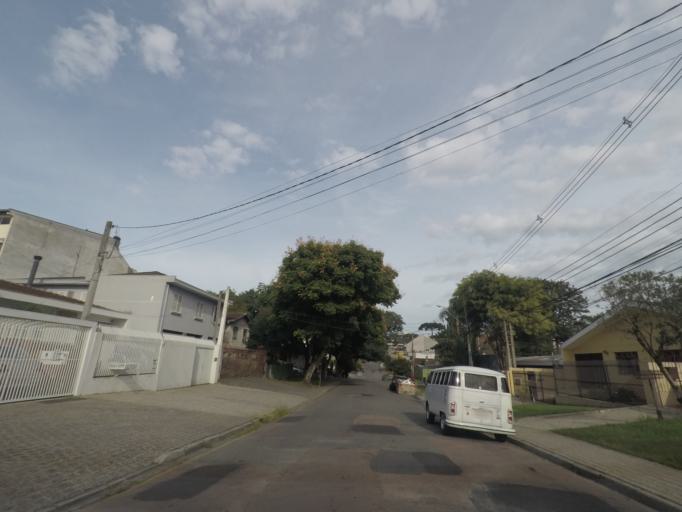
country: BR
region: Parana
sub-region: Curitiba
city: Curitiba
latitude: -25.4289
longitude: -49.2973
